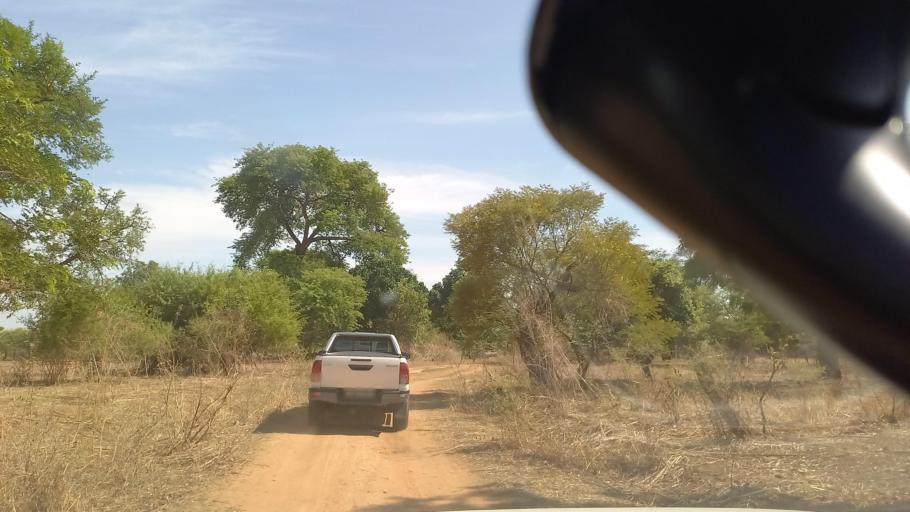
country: ZM
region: Southern
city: Mazabuka
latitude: -16.0331
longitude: 27.6236
